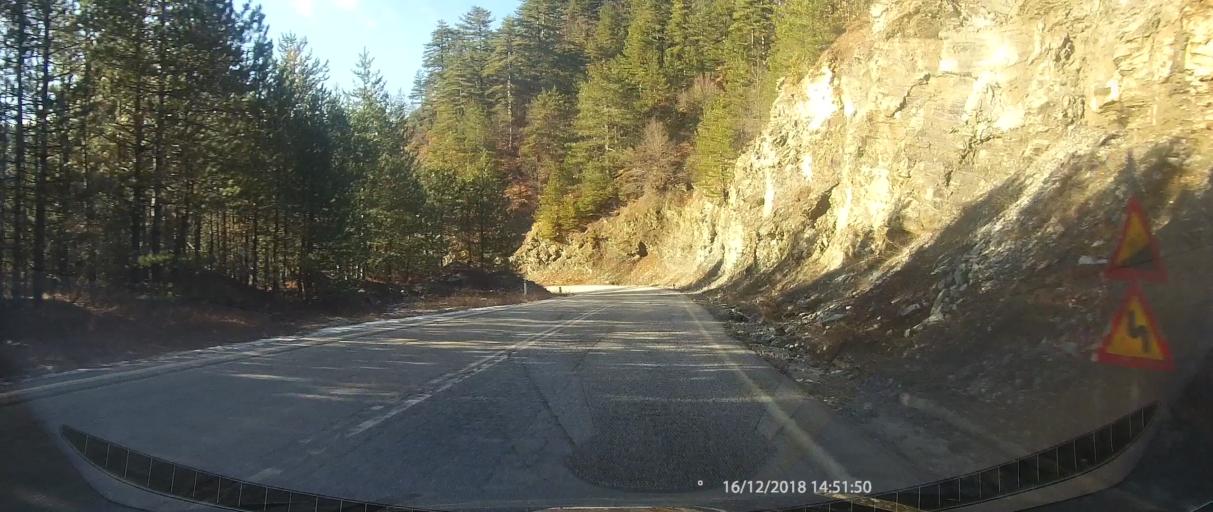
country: GR
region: West Macedonia
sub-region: Nomos Kastorias
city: Nestorio
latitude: 40.2044
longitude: 21.0683
